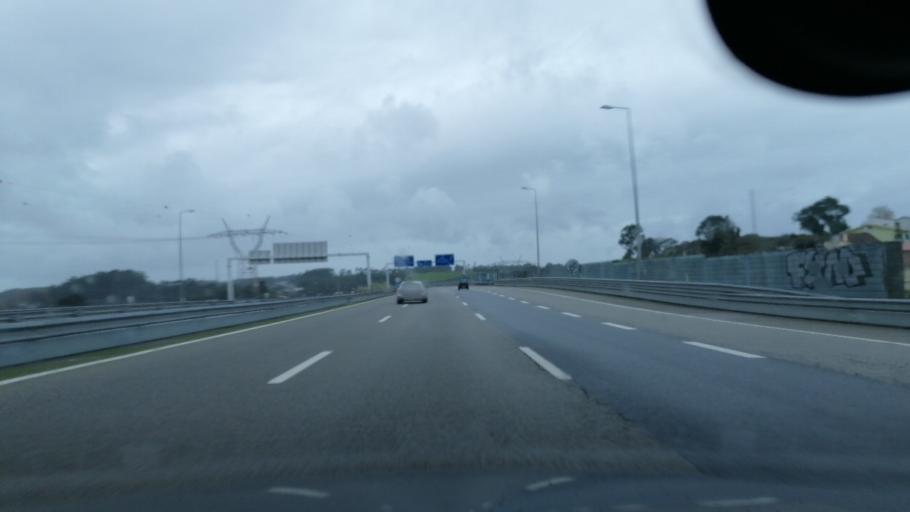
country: PT
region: Porto
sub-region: Matosinhos
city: Guifoes
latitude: 41.2127
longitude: -8.6531
